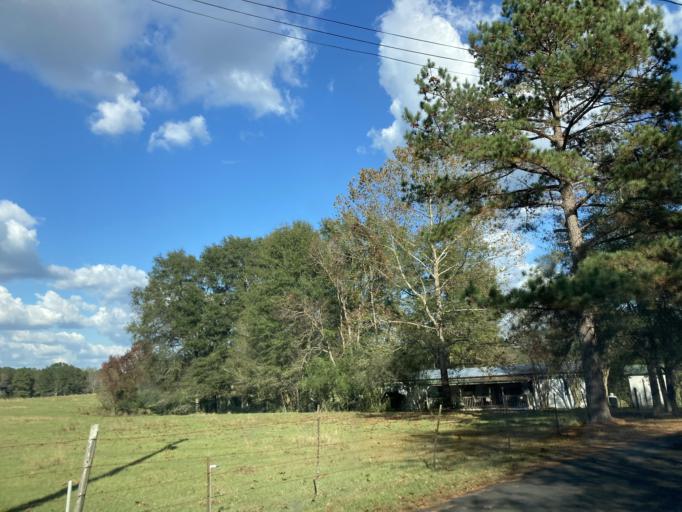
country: US
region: Mississippi
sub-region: Lamar County
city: Sumrall
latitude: 31.4156
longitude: -89.6230
